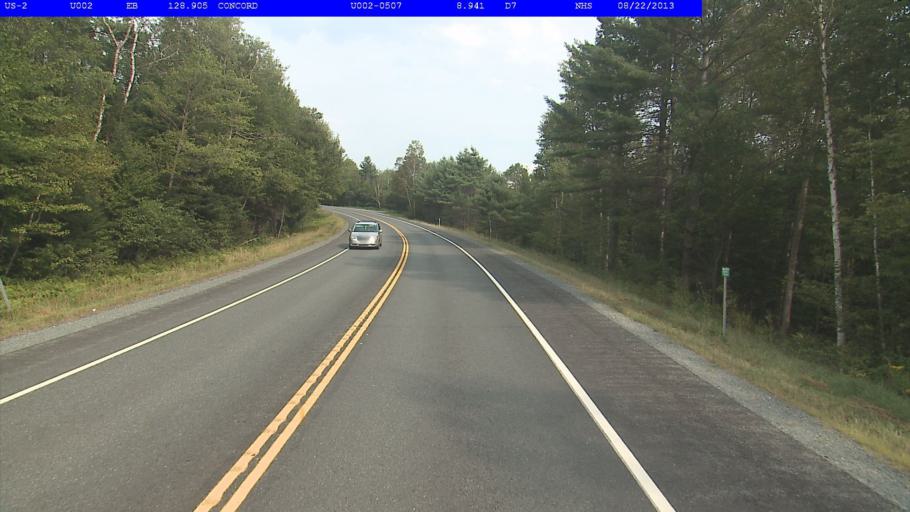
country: US
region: New Hampshire
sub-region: Grafton County
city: Littleton
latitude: 44.4497
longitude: -71.7978
